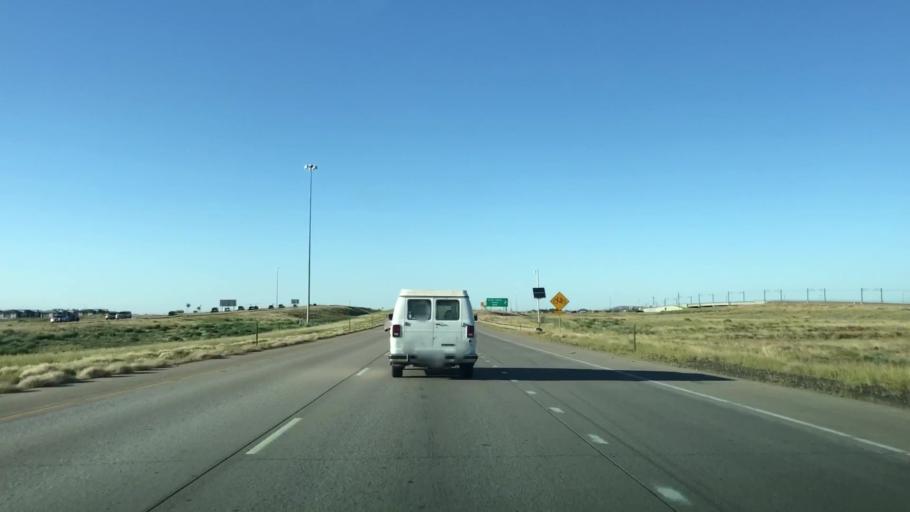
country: US
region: Colorado
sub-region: Adams County
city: Aurora
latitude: 39.7778
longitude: -104.7905
